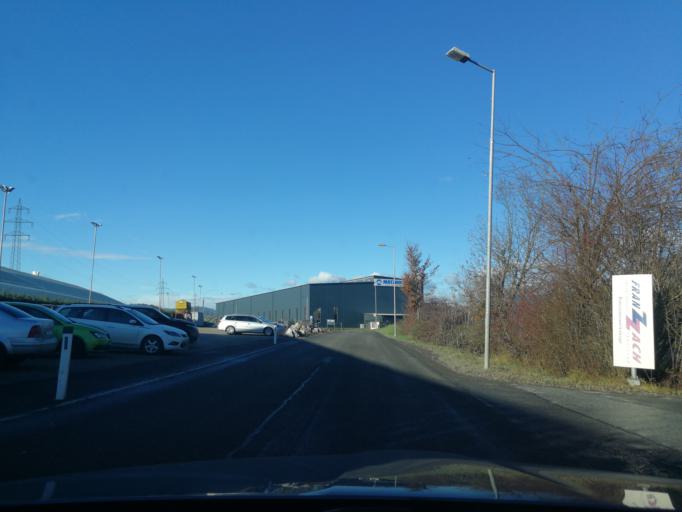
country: AT
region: Styria
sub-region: Politischer Bezirk Weiz
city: Gleisdorf
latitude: 47.1165
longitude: 15.6982
